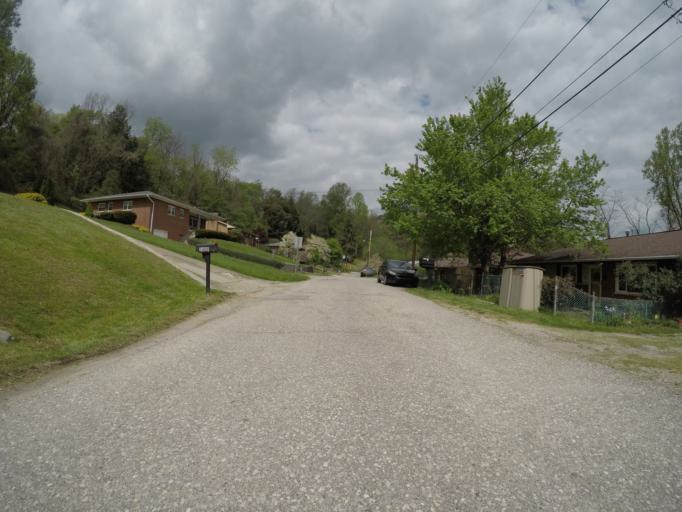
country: US
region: West Virginia
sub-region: Kanawha County
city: Charleston
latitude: 38.3904
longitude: -81.6035
